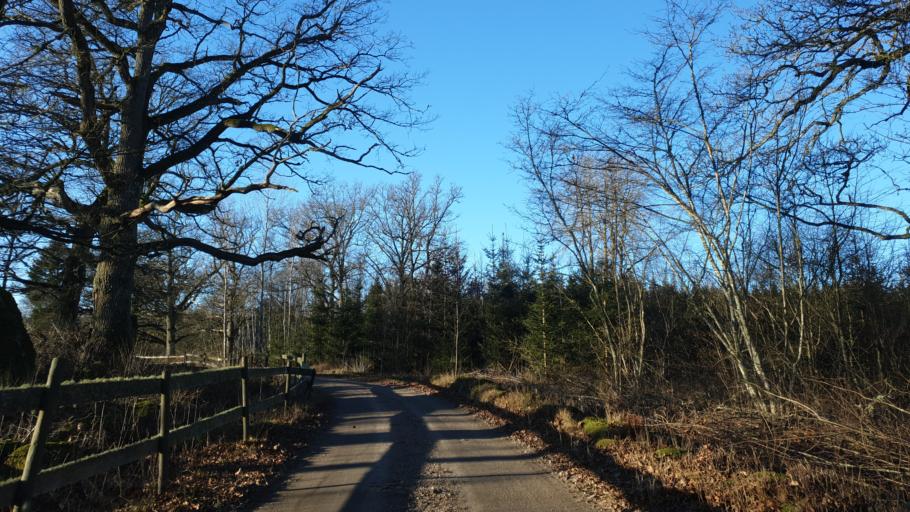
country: SE
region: Blekinge
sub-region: Karlskrona Kommun
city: Nattraby
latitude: 56.2591
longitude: 15.4175
